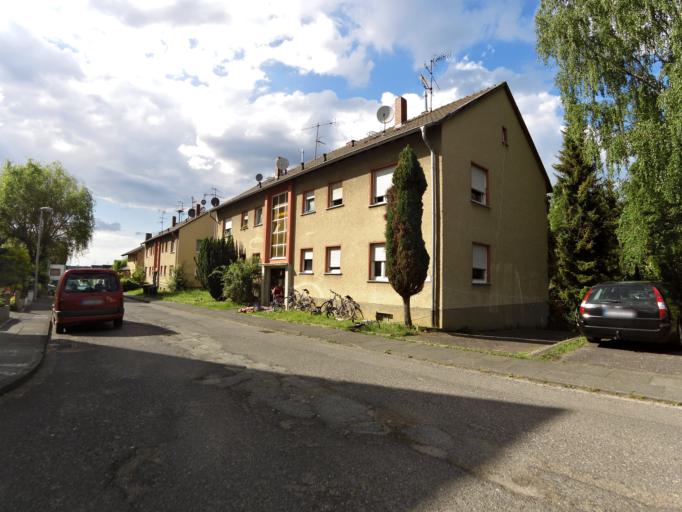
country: DE
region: North Rhine-Westphalia
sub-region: Regierungsbezirk Koln
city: Alfter
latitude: 50.6897
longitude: 7.0336
